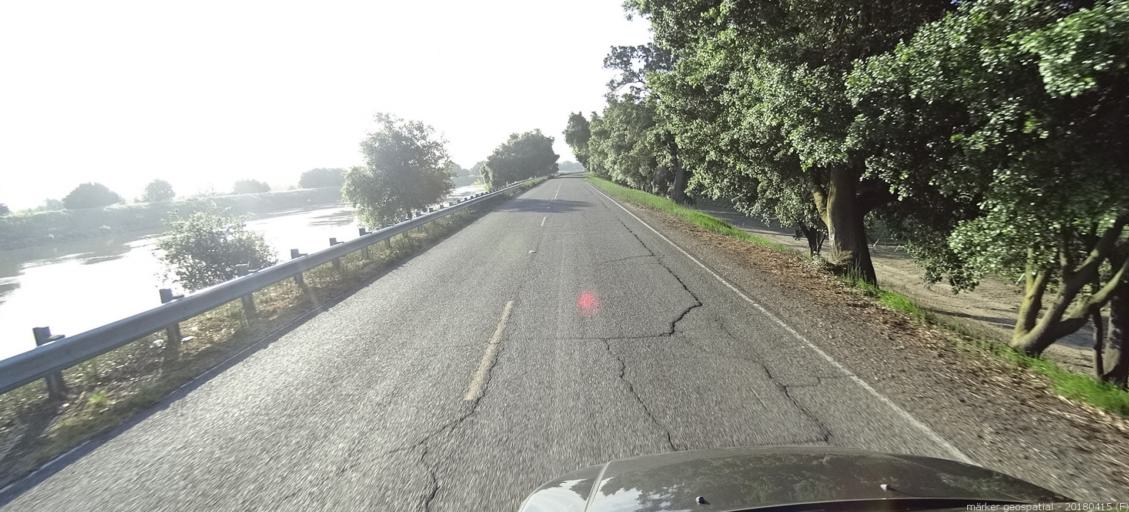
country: US
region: California
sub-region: Sacramento County
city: Walnut Grove
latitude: 38.2826
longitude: -121.5517
